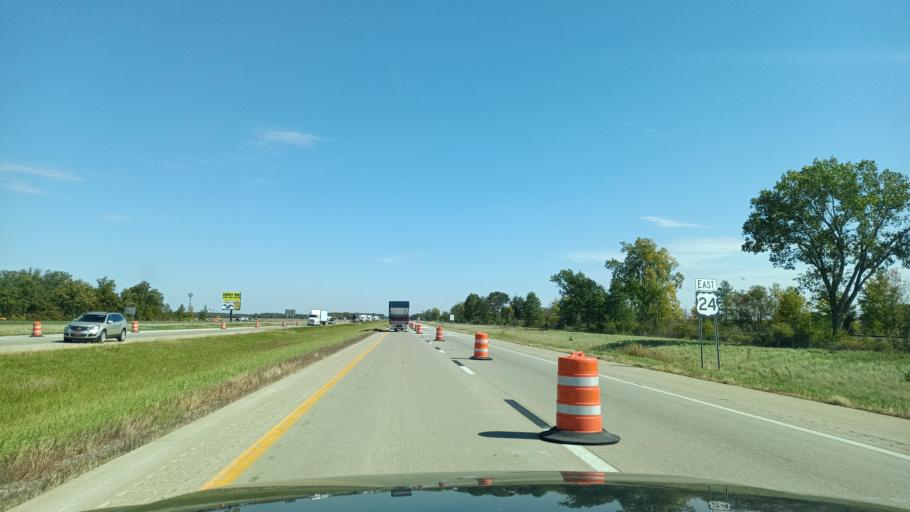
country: US
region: Ohio
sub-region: Defiance County
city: Defiance
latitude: 41.2517
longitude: -84.4750
